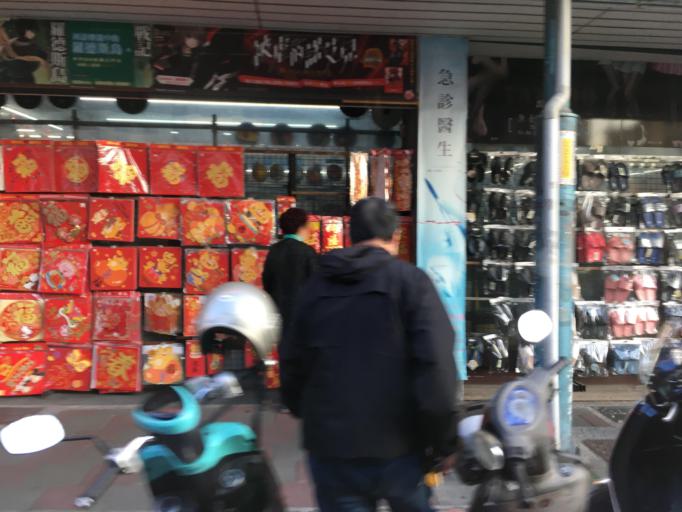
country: TW
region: Taipei
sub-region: Taipei
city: Banqiao
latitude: 25.0447
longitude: 121.4533
